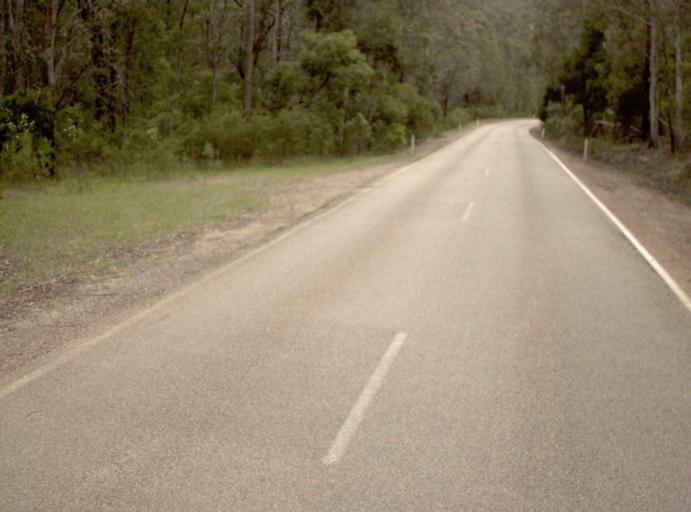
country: AU
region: Victoria
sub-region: East Gippsland
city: Bairnsdale
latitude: -37.6264
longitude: 147.2091
